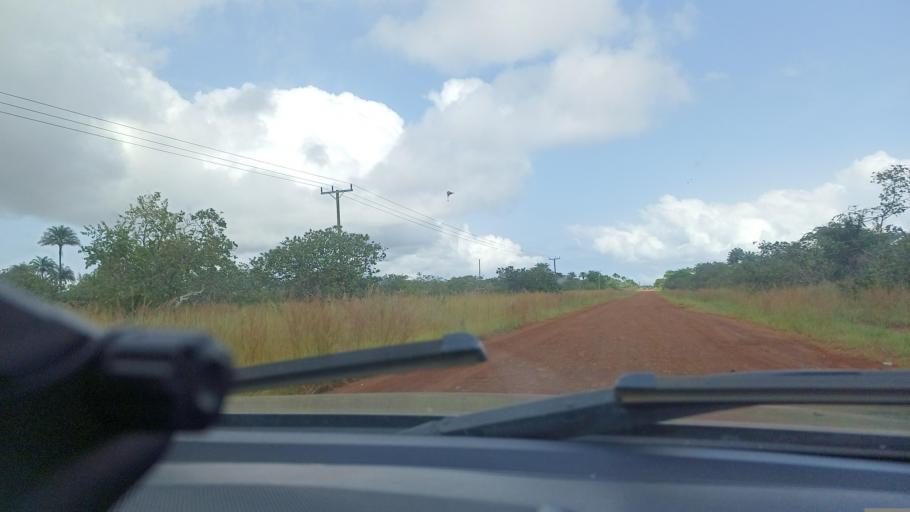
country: LR
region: Grand Cape Mount
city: Robertsport
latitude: 6.6935
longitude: -11.2824
